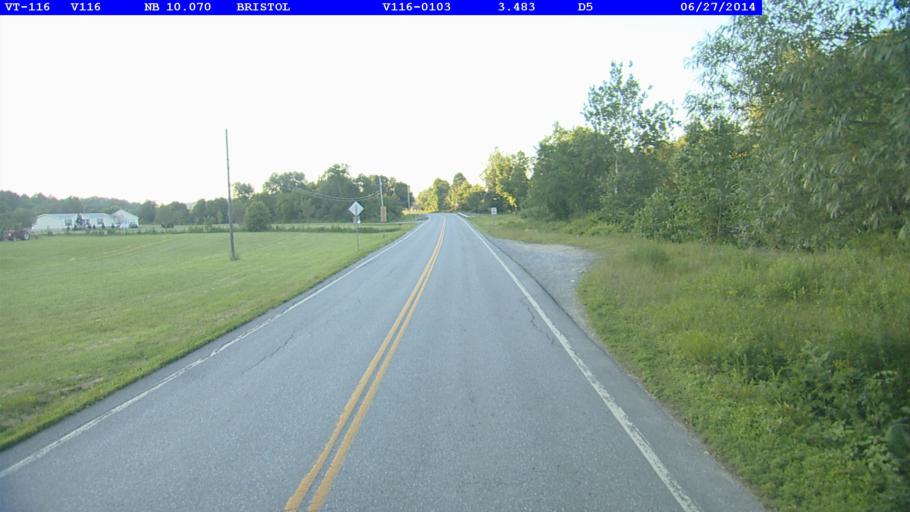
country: US
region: Vermont
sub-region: Addison County
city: Bristol
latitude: 44.1007
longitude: -73.0969
